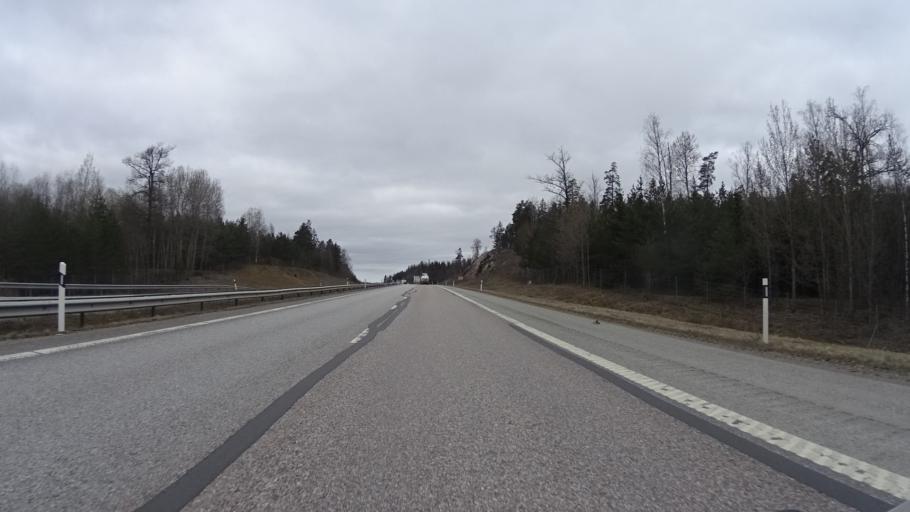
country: SE
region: Soedermanland
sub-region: Strangnas Kommun
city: Strangnas
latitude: 59.3693
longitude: 16.8507
